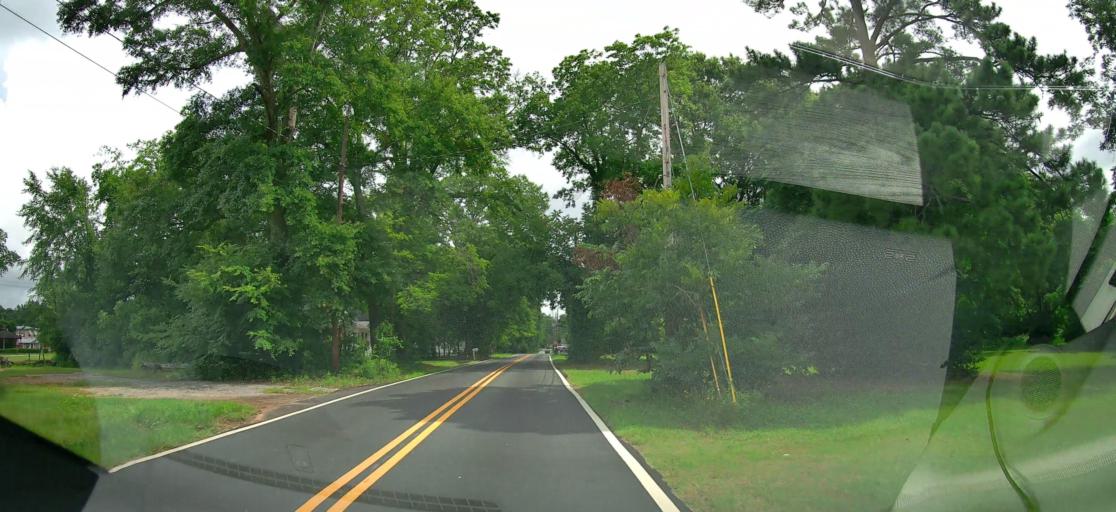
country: US
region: Georgia
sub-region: Peach County
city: Byron
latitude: 32.6519
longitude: -83.7588
